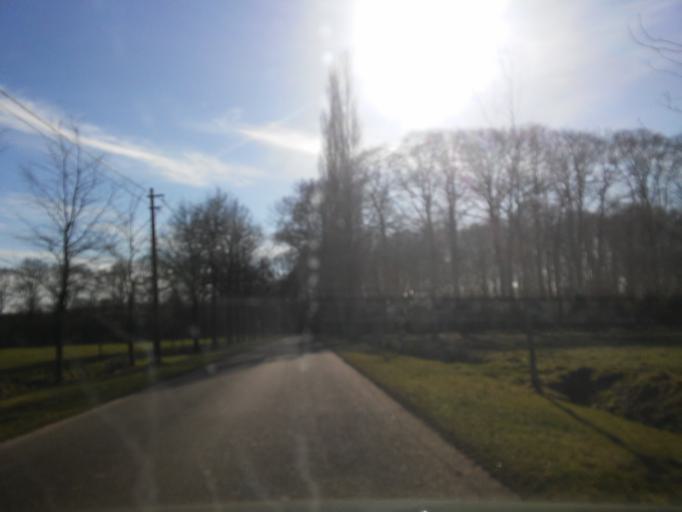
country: BE
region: Flanders
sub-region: Provincie Oost-Vlaanderen
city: Maldegem
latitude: 51.1560
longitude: 3.4757
